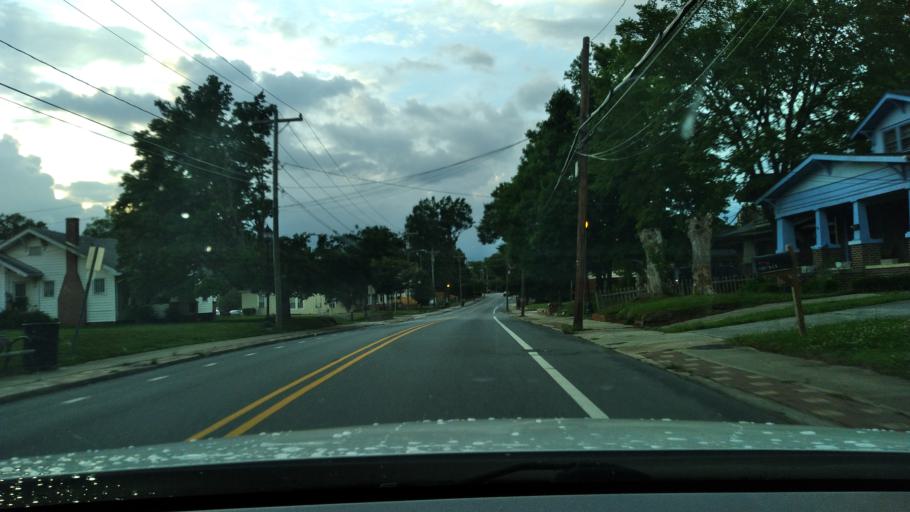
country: US
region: North Carolina
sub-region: Guilford County
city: Greensboro
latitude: 36.0542
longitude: -79.7831
